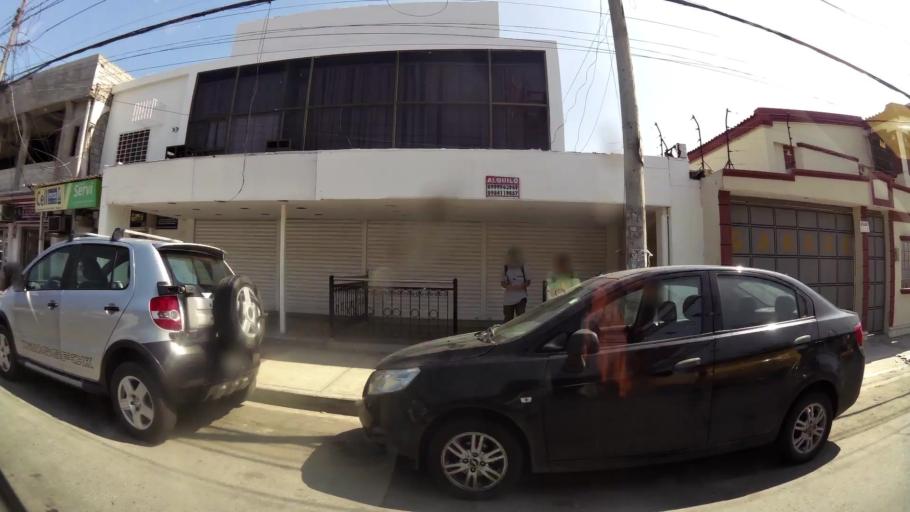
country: EC
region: Guayas
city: Guayaquil
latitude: -2.1691
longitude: -79.9104
